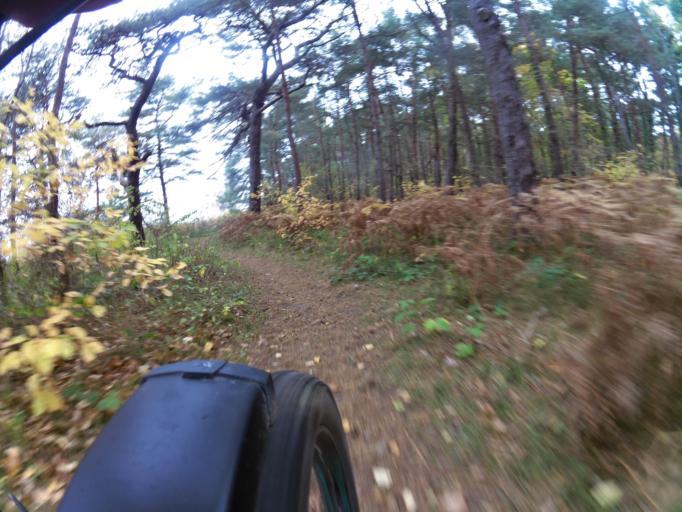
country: PL
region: Pomeranian Voivodeship
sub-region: Powiat pucki
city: Jastarnia
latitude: 54.6852
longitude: 18.7066
